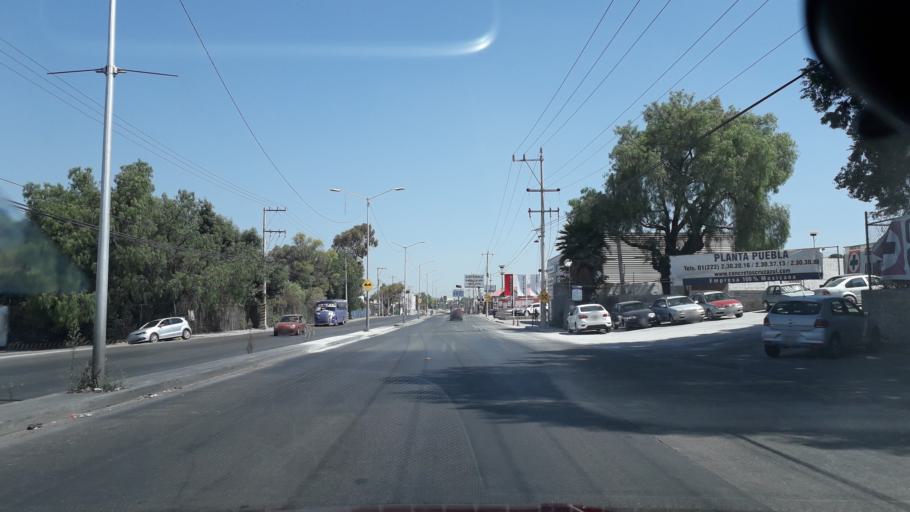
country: MX
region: Puebla
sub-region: Cuautlancingo
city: Sanctorum
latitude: 19.0802
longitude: -98.2389
